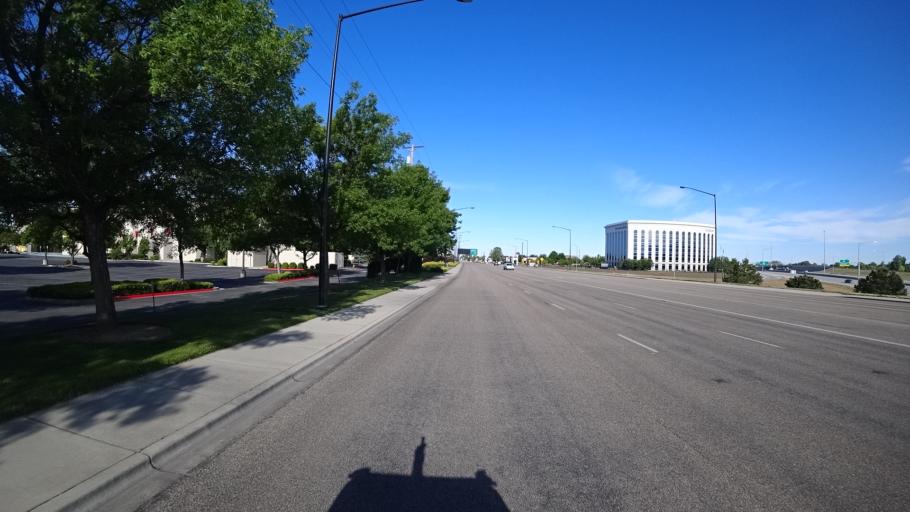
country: US
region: Idaho
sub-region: Ada County
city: Garden City
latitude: 43.5901
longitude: -116.2761
